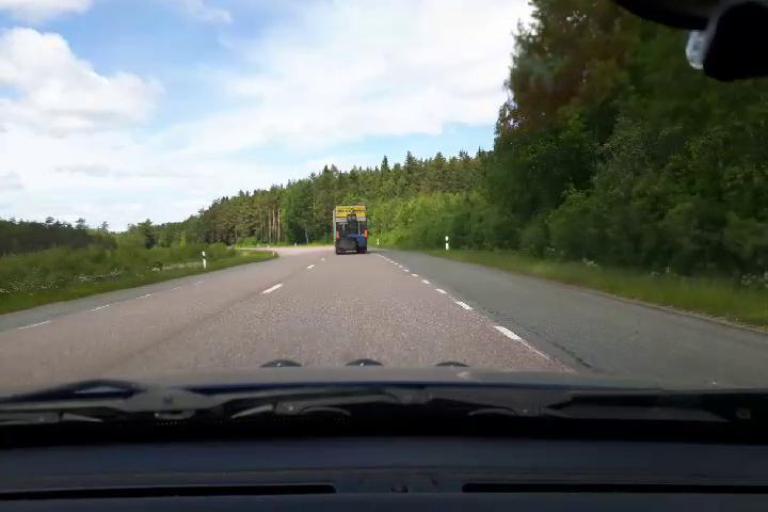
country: SE
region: Uppsala
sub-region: Osthammars Kommun
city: Bjorklinge
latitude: 60.0994
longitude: 17.5534
